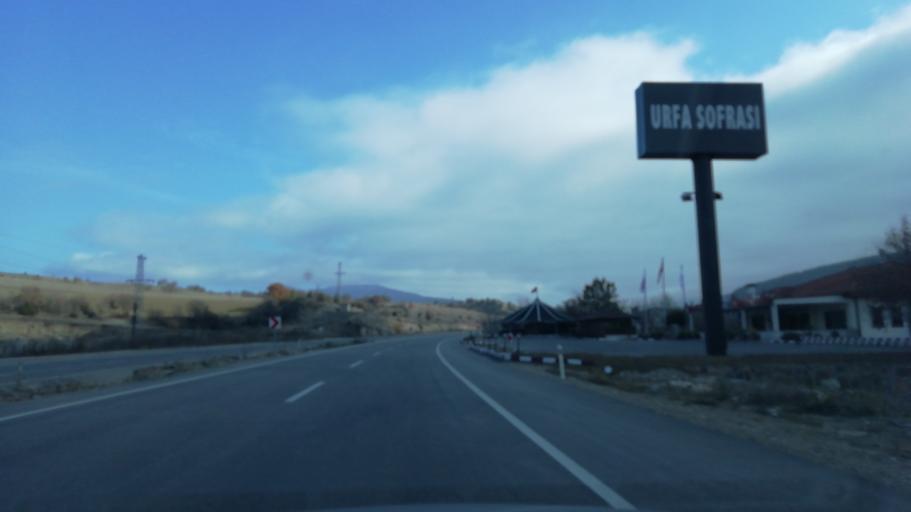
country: TR
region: Karabuk
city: Safranbolu
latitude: 41.2182
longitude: 32.7436
